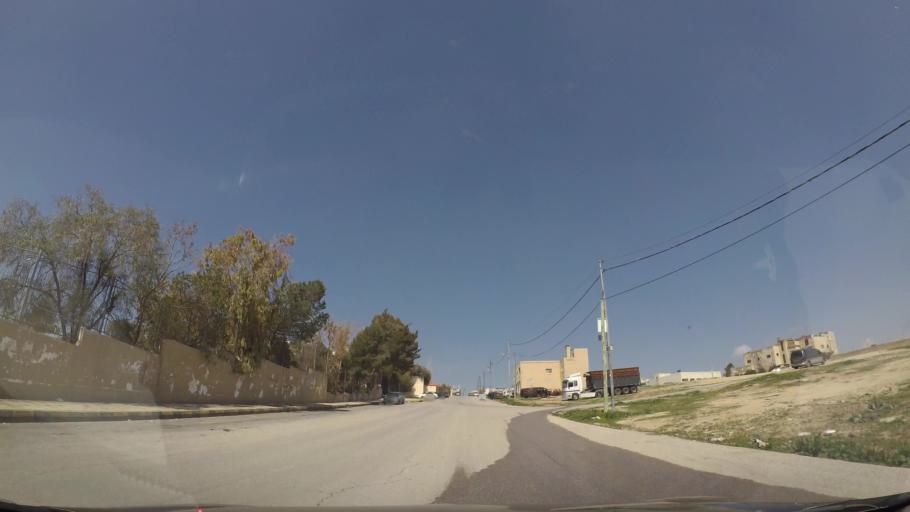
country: JO
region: Amman
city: Amman
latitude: 31.9787
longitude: 35.9990
